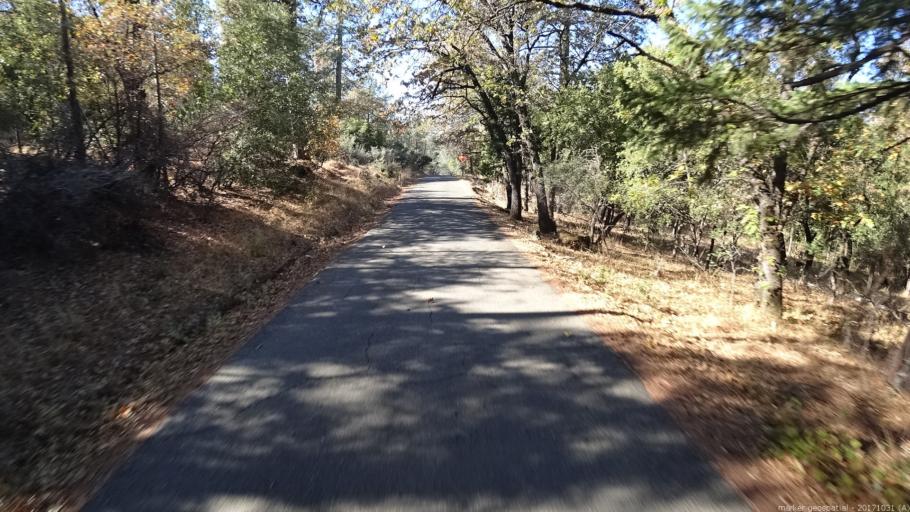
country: US
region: California
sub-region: Shasta County
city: Shingletown
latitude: 40.5240
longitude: -121.9552
